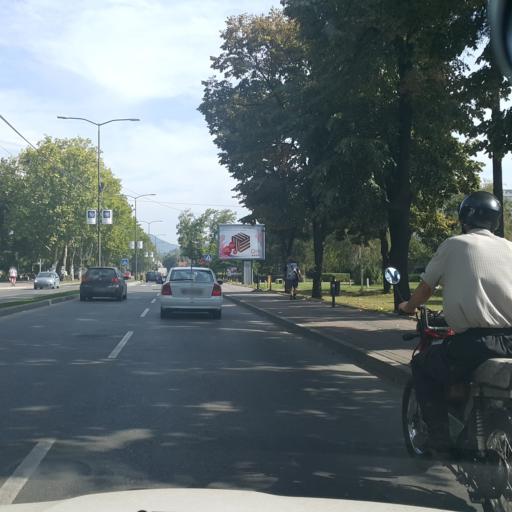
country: RS
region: Central Serbia
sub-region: Nisavski Okrug
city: Nis
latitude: 43.3165
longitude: 21.9139
